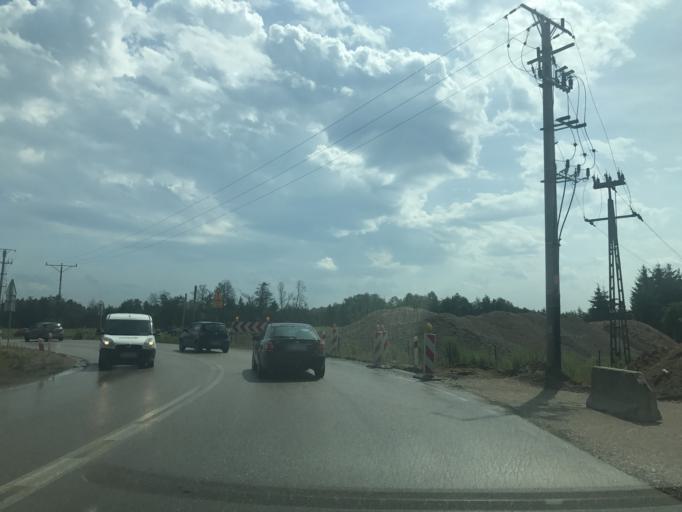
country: PL
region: Warmian-Masurian Voivodeship
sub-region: Powiat ostrodzki
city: Ostroda
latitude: 53.7148
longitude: 19.9601
